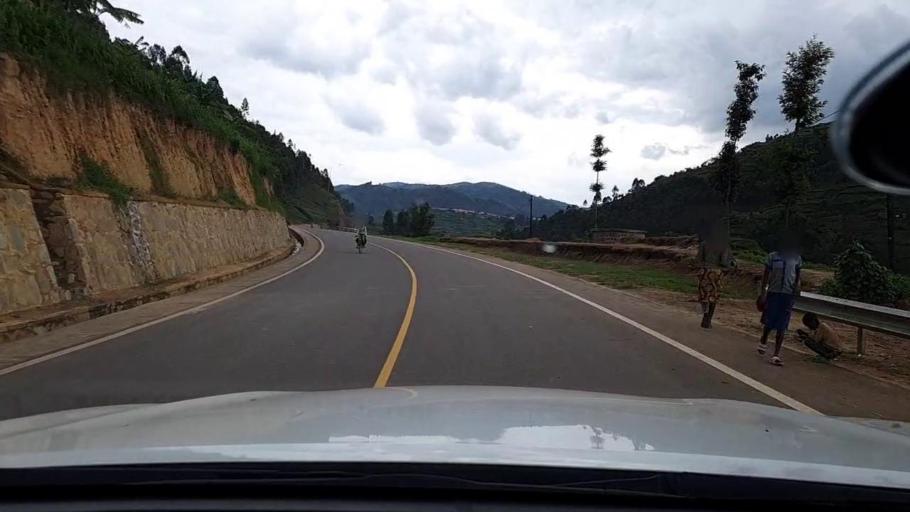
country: RW
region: Northern Province
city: Byumba
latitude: -1.6440
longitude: 29.9250
